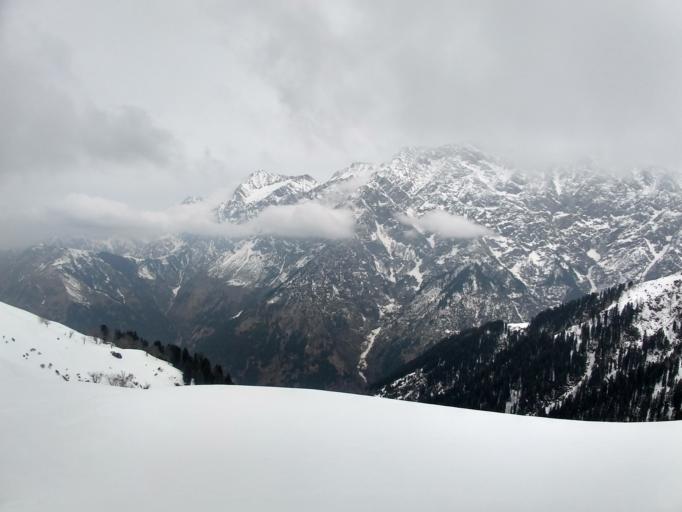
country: IN
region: Himachal Pradesh
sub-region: Kangra
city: Palampur
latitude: 32.1818
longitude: 76.5089
